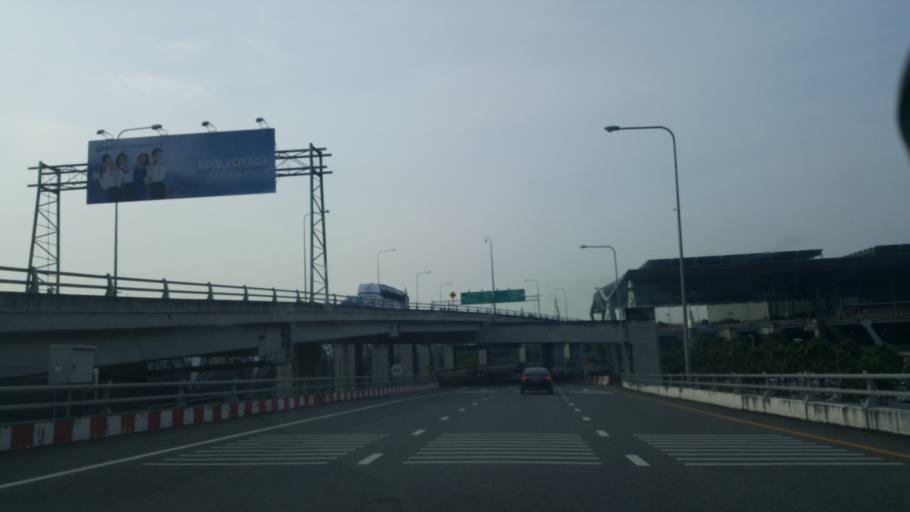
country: TH
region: Bangkok
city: Lat Krabang
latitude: 13.6949
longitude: 100.7544
